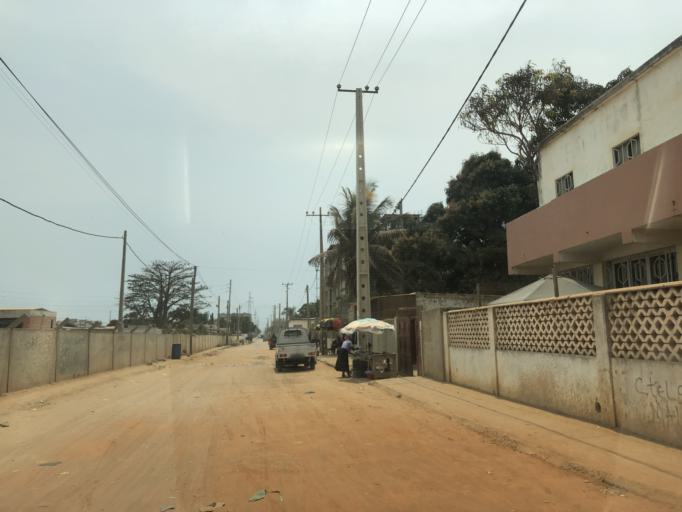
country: AO
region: Luanda
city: Luanda
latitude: -8.8880
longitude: 13.1917
